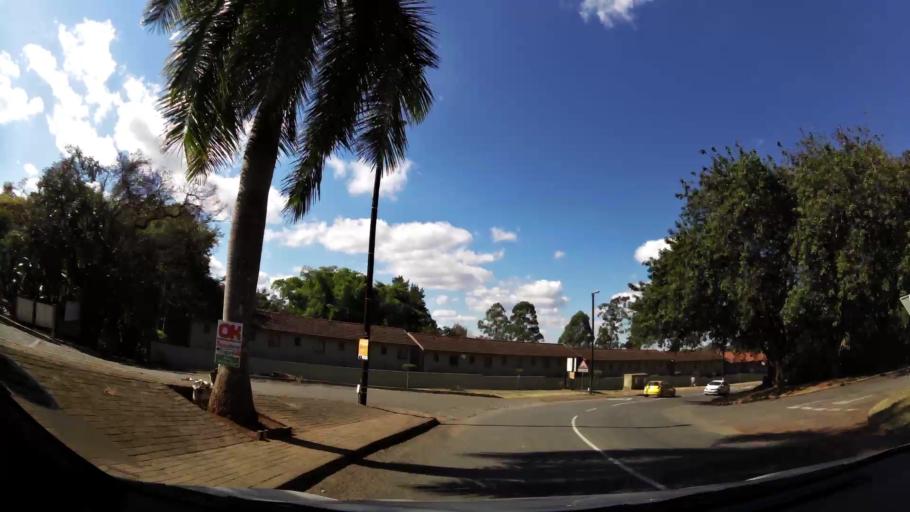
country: ZA
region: Limpopo
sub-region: Mopani District Municipality
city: Tzaneen
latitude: -23.8273
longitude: 30.1493
